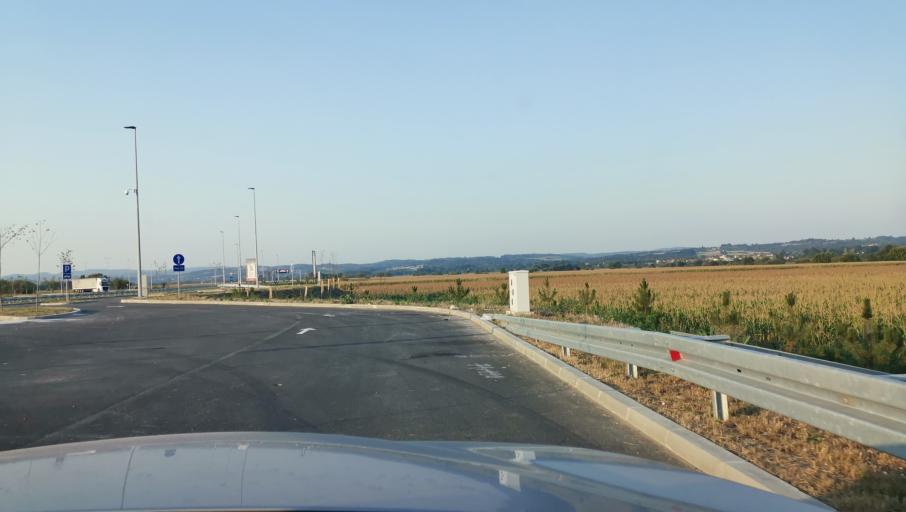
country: RS
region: Central Serbia
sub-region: Kolubarski Okrug
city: Ljig
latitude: 44.2413
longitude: 20.2630
